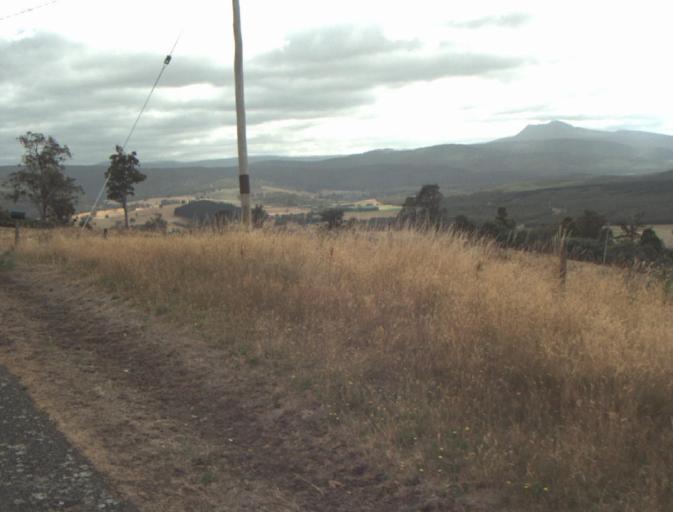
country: AU
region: Tasmania
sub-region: Northern Midlands
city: Evandale
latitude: -41.5150
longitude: 147.4713
